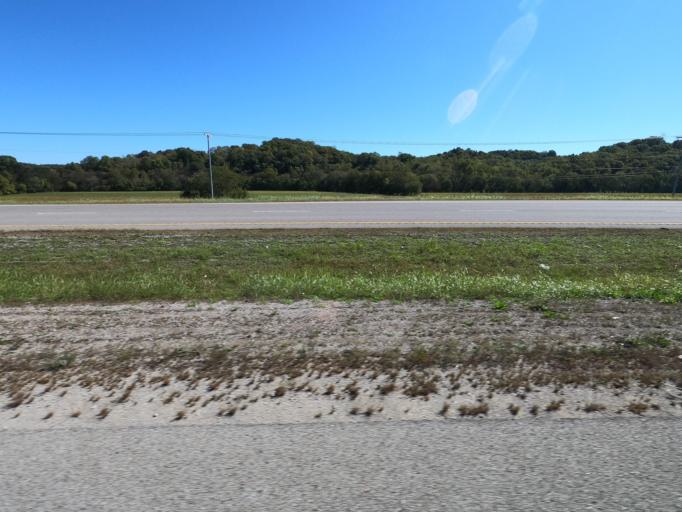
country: US
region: Tennessee
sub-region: Maury County
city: Mount Pleasant
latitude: 35.4929
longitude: -87.2351
